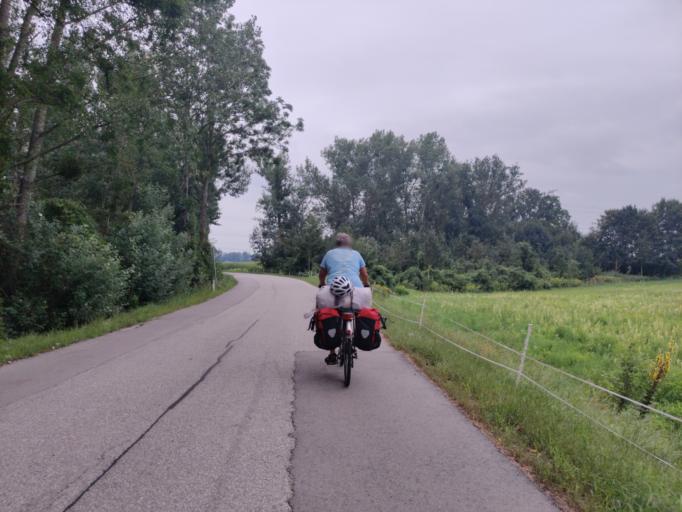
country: AT
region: Lower Austria
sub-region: Politischer Bezirk Tulln
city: Langenrohr
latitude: 48.3301
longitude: 15.9962
